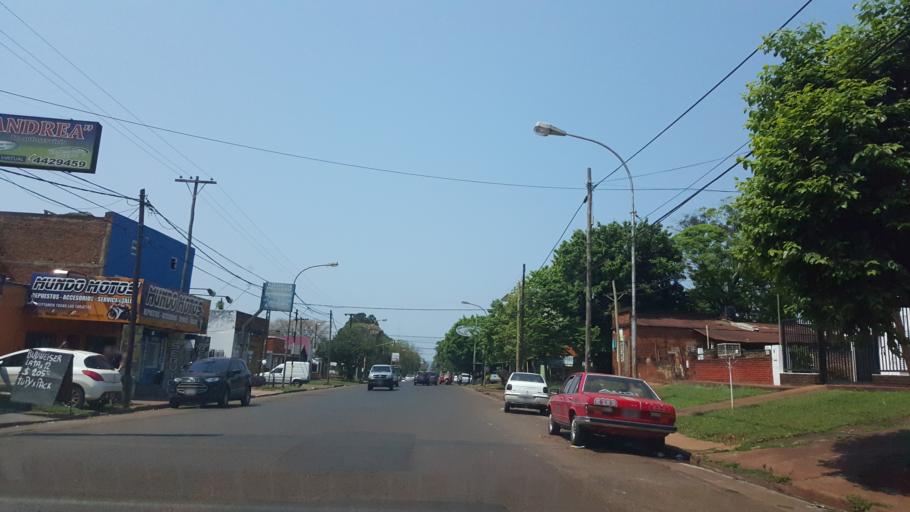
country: AR
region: Misiones
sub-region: Departamento de Capital
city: Posadas
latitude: -27.3834
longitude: -55.9085
